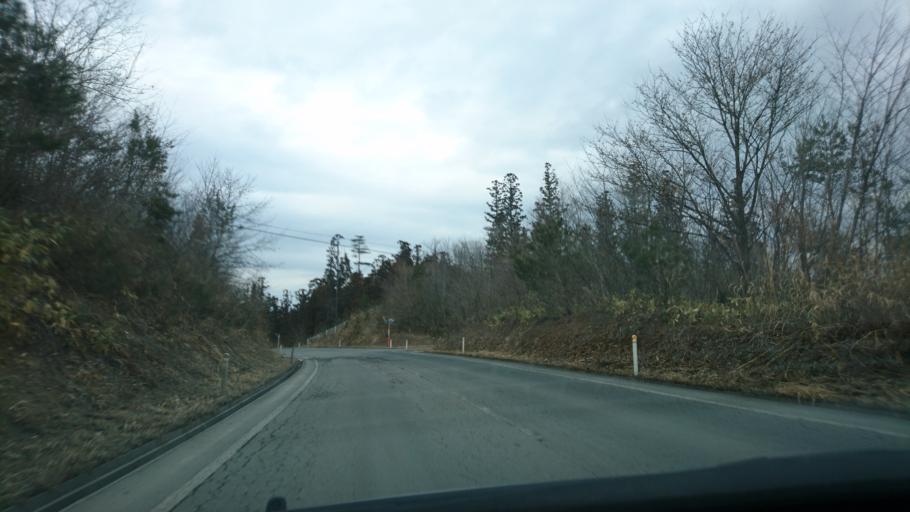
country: JP
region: Iwate
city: Ichinoseki
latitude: 38.9888
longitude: 141.3575
